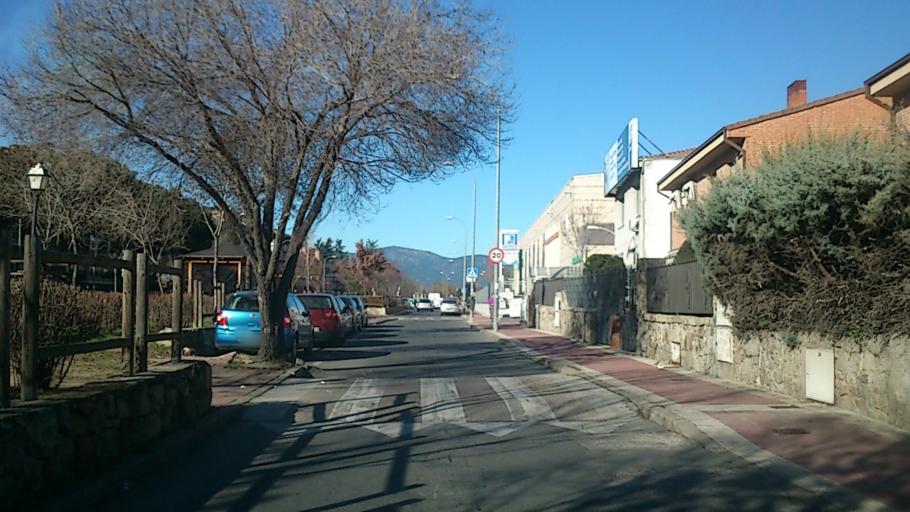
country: ES
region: Madrid
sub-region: Provincia de Madrid
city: Collado-Villalba
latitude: 40.6355
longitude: -4.0155
